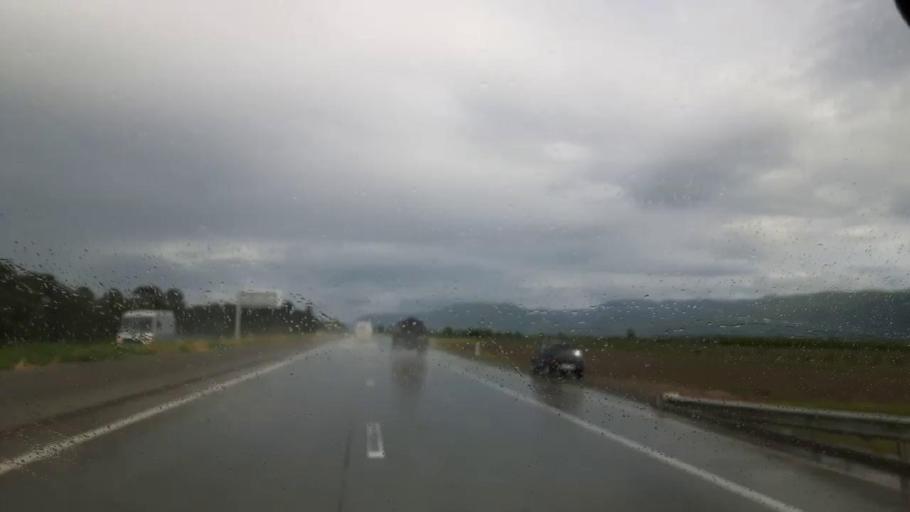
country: GE
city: Agara
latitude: 42.0415
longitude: 43.9282
